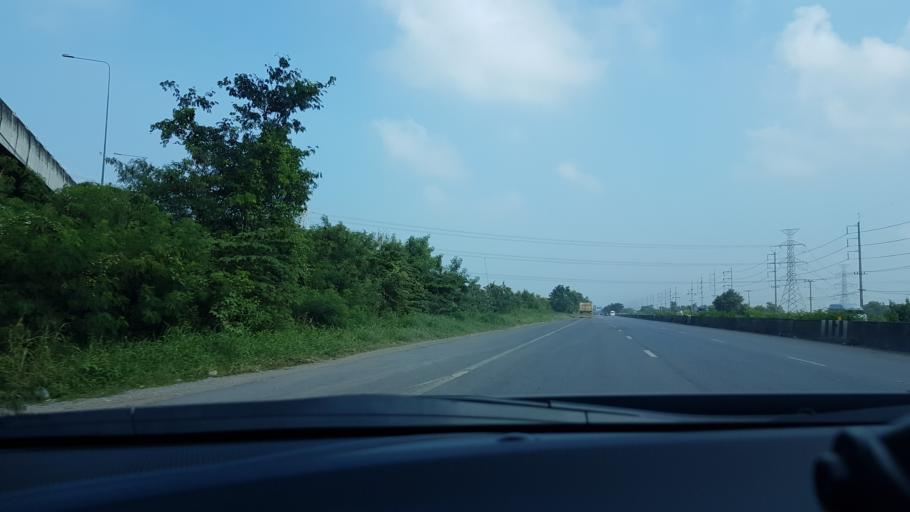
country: TH
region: Pathum Thani
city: Sam Khok
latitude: 14.1287
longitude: 100.5696
